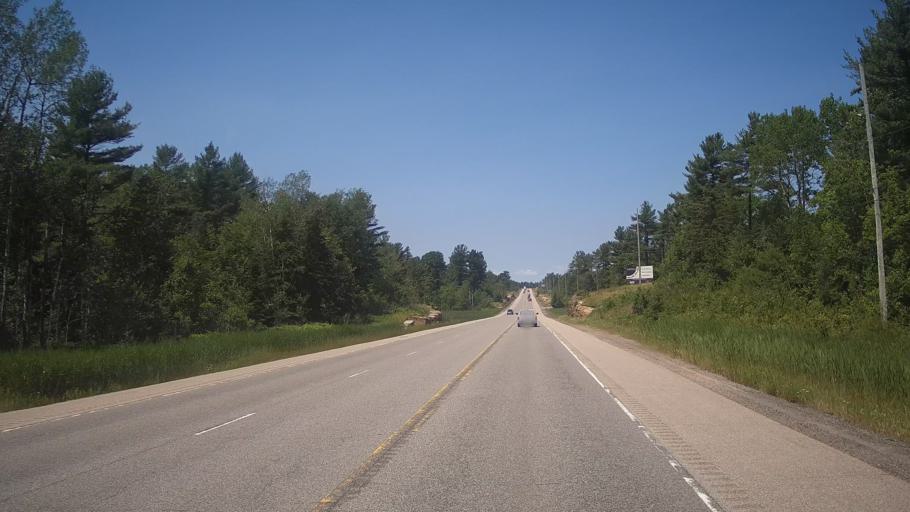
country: CA
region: Ontario
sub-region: Parry Sound District
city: Parry Sound
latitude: 45.6703
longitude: -80.4288
